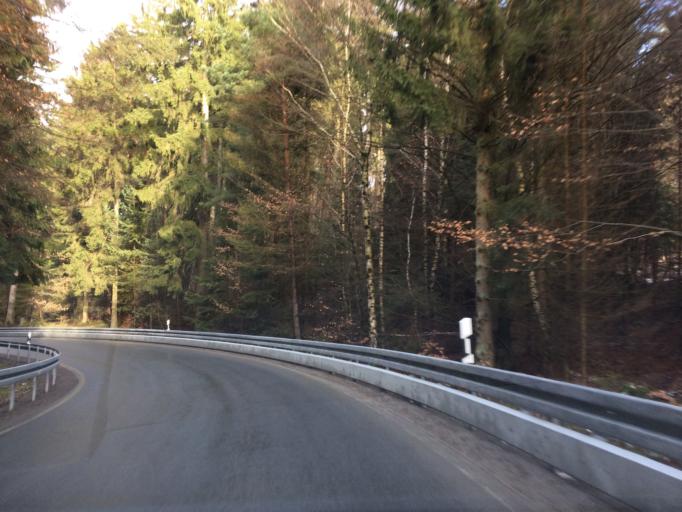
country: DE
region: Hesse
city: Bad Camberg
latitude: 50.3264
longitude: 8.3387
